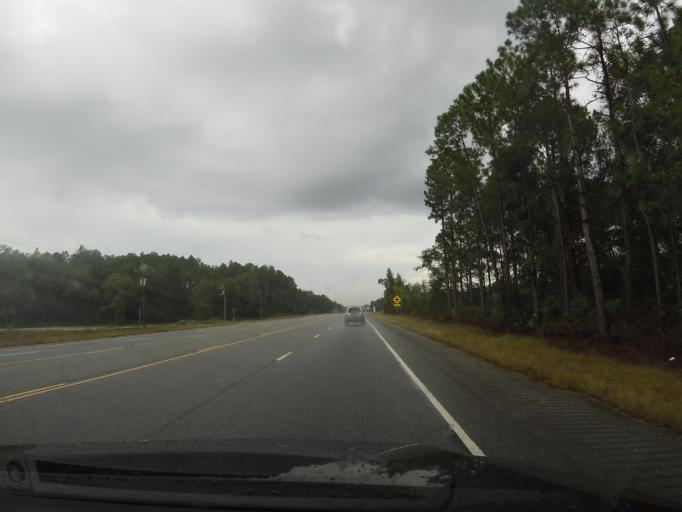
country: US
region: Georgia
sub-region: Wayne County
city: Jesup
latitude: 31.5764
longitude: -81.8481
